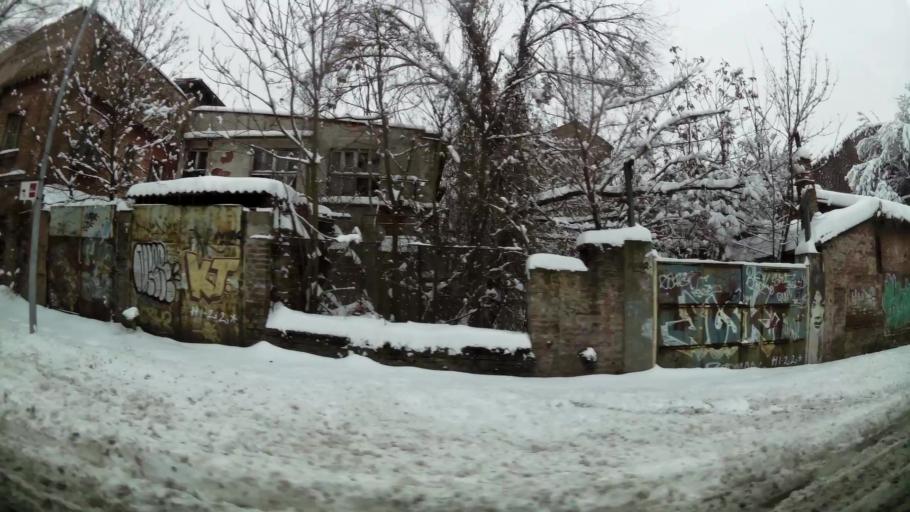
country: RS
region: Central Serbia
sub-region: Belgrade
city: Stari Grad
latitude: 44.8189
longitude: 20.4841
